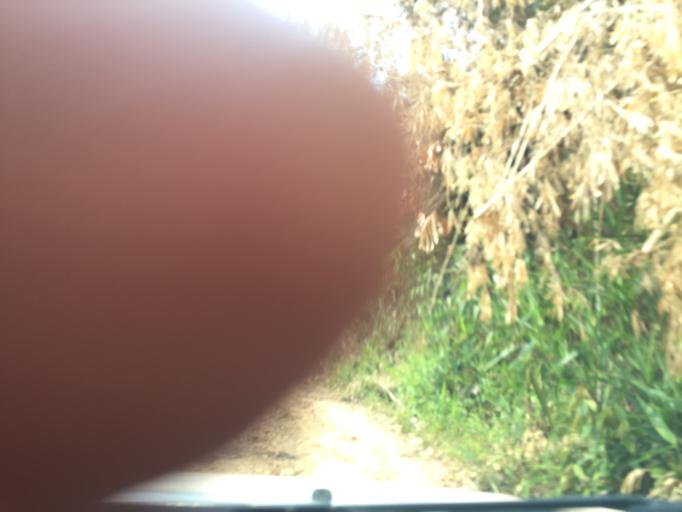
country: LA
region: Loungnamtha
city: Muang Nale
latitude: 20.6202
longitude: 101.6126
